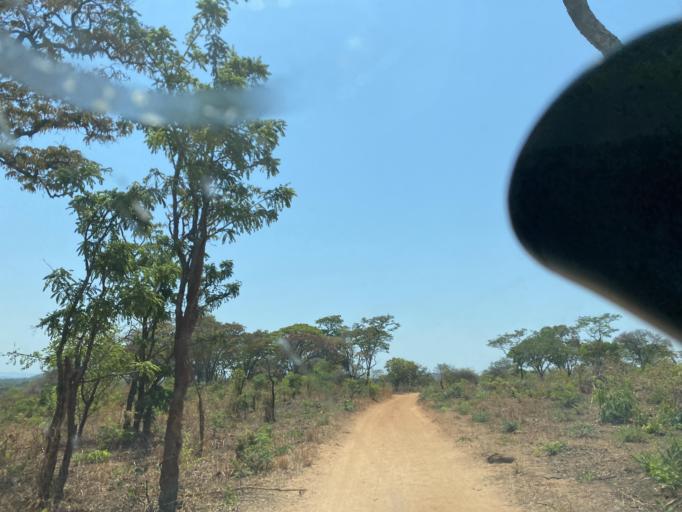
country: ZM
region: Lusaka
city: Chongwe
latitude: -15.4228
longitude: 29.1783
